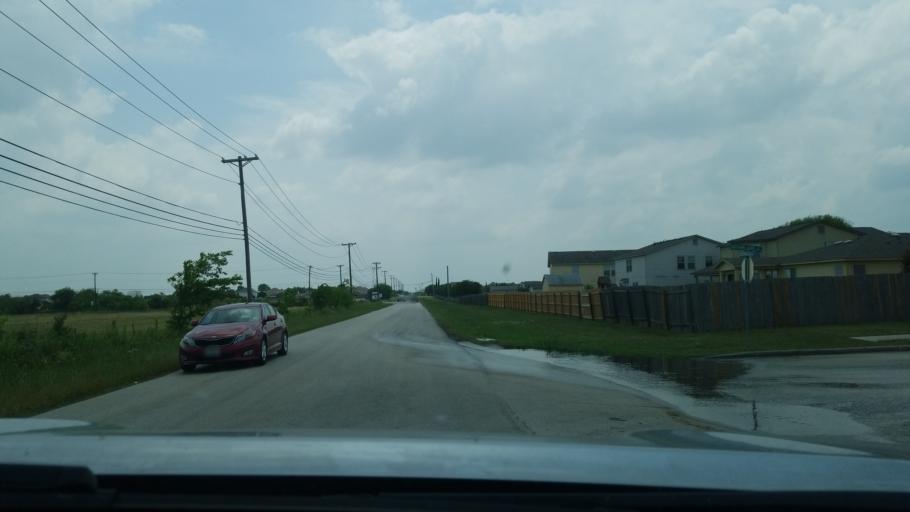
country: US
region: Texas
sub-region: Comal County
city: New Braunfels
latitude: 29.7567
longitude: -98.0653
